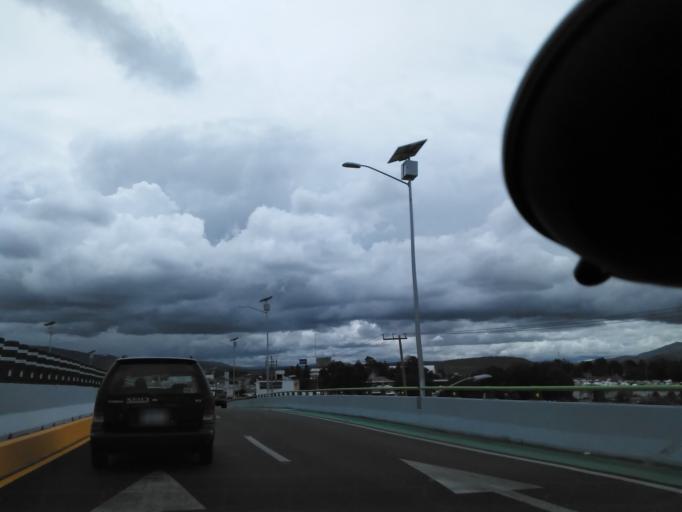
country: MX
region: Hidalgo
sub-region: Tula de Allende
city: Residencial Arboledas
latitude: 20.0539
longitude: -99.3109
